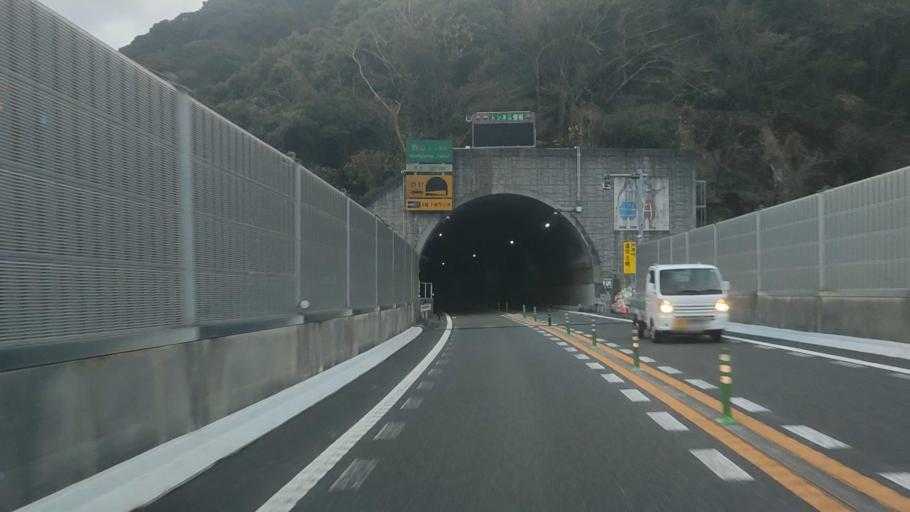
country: JP
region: Nagasaki
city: Obita
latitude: 32.7922
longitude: 129.8816
